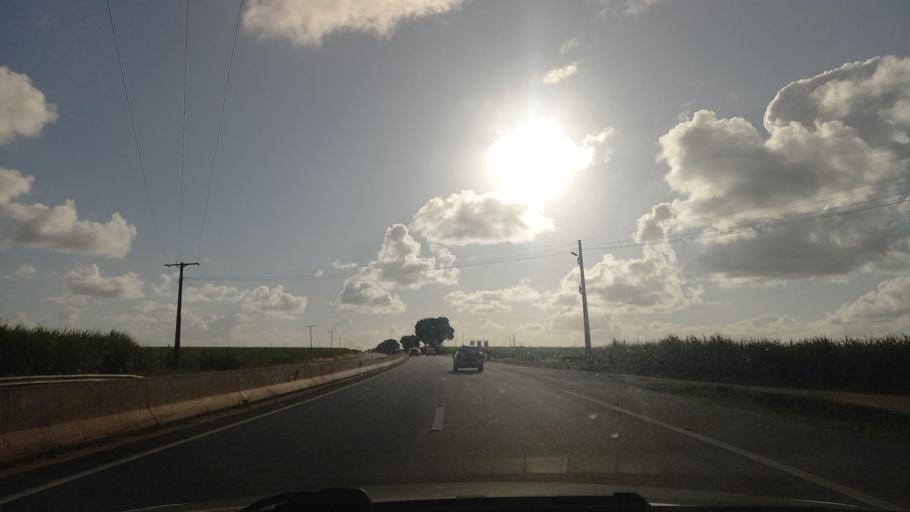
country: BR
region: Alagoas
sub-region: Sao Miguel Dos Campos
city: Sao Miguel dos Campos
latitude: -9.8061
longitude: -36.1217
